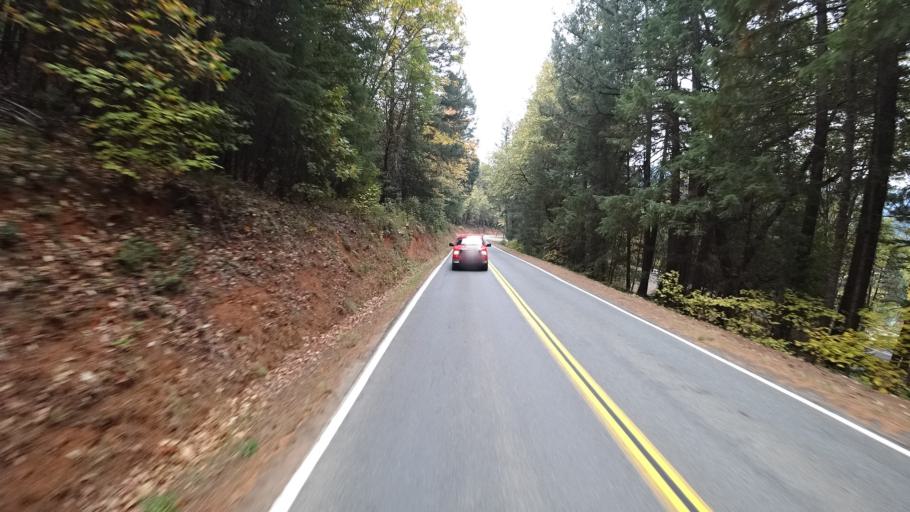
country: US
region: California
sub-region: Siskiyou County
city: Happy Camp
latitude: 41.8090
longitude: -123.3804
